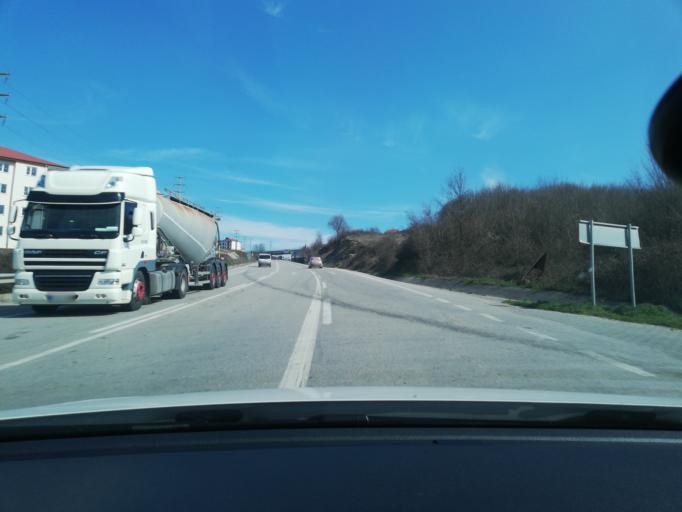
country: TR
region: Duzce
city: Akcakoca
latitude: 41.0793
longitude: 31.1291
